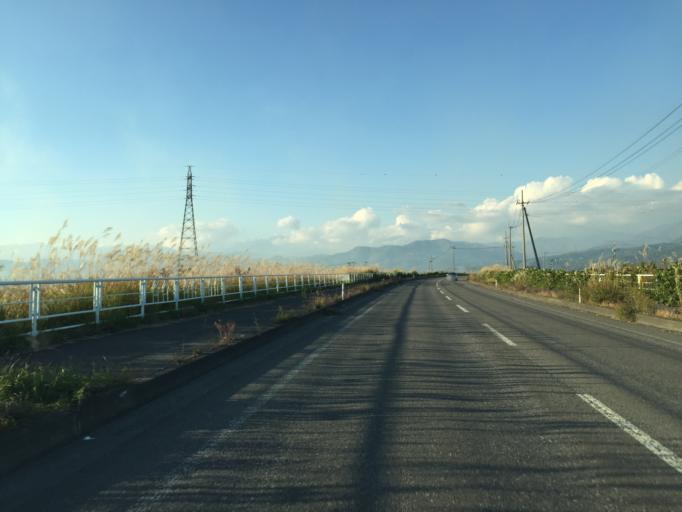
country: JP
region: Fukushima
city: Kitakata
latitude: 37.6736
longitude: 139.8883
